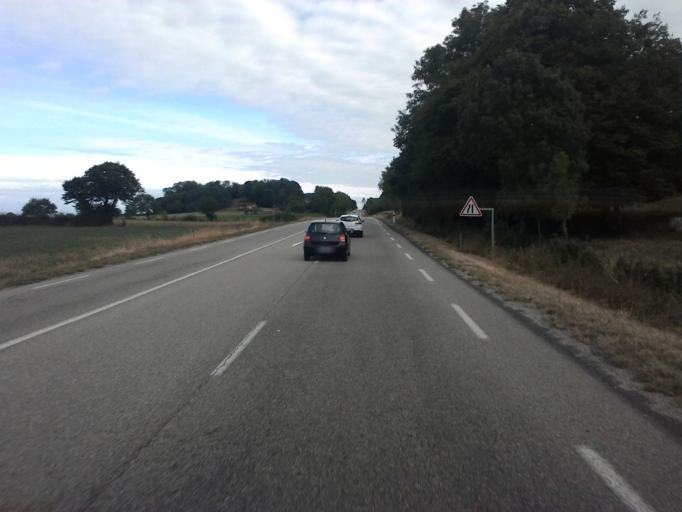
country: FR
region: Rhone-Alpes
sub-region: Departement de l'Ain
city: Saint-Martin-du-Mont
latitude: 46.0765
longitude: 5.3221
